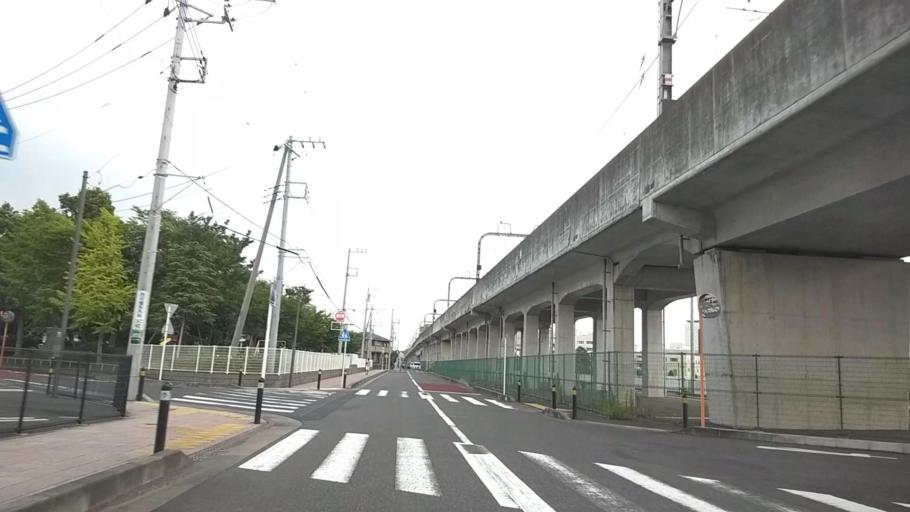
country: JP
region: Kanagawa
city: Atsugi
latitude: 35.4452
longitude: 139.3816
